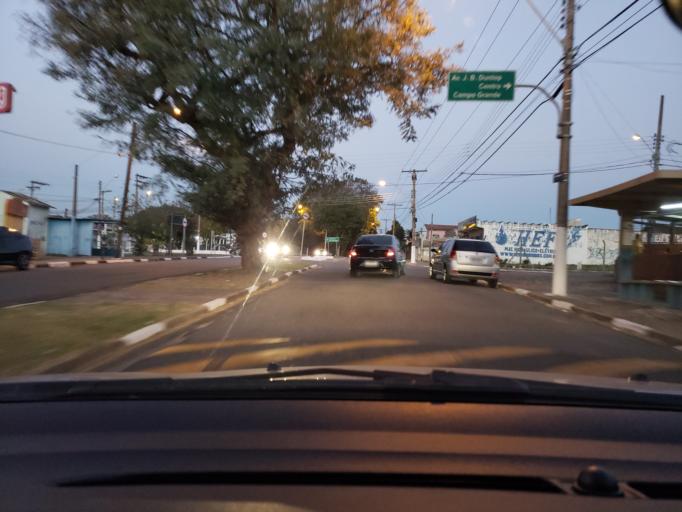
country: BR
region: Sao Paulo
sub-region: Campinas
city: Campinas
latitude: -22.9170
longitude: -47.1121
